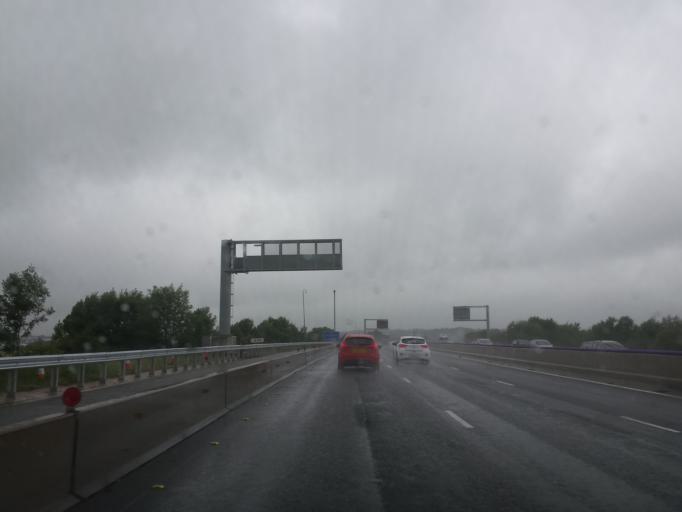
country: GB
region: England
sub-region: Derbyshire
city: Blackwell
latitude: 53.1279
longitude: -1.3293
